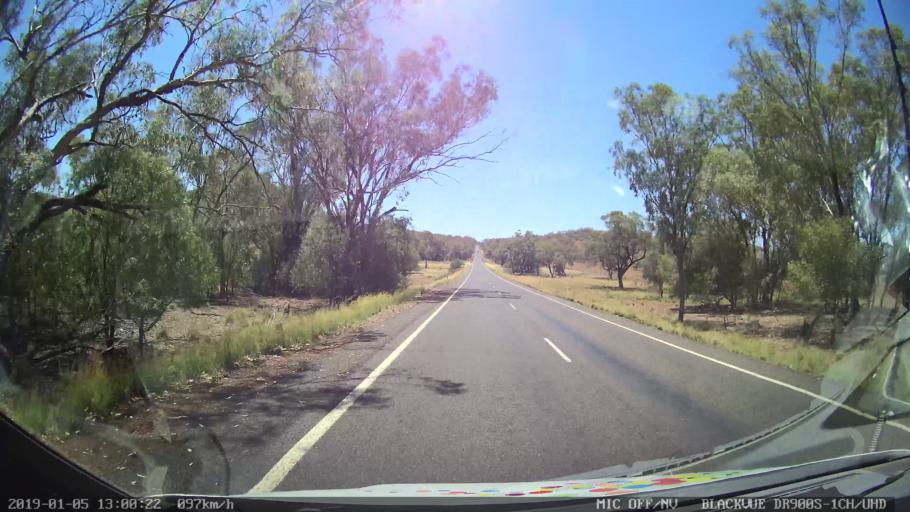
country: AU
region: New South Wales
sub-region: Narrabri
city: Boggabri
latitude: -31.1152
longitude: 149.7807
